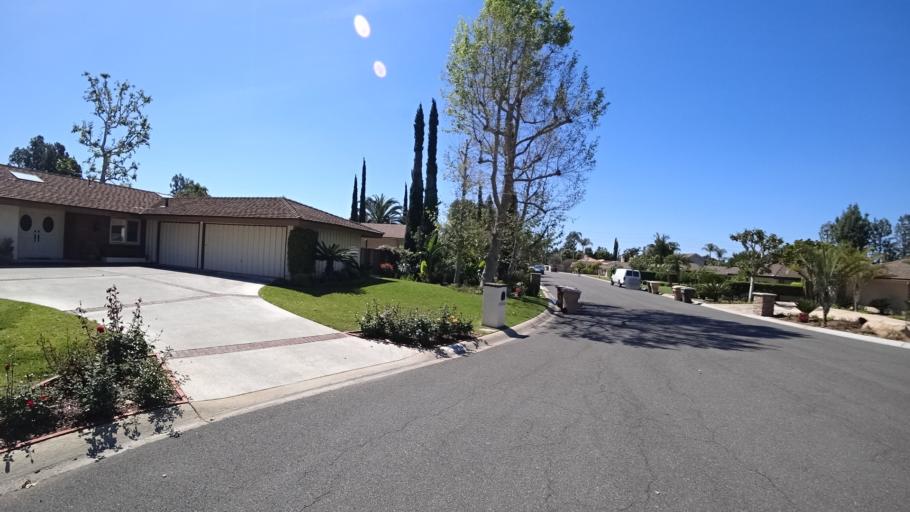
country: US
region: California
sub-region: Orange County
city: Villa Park
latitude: 33.8158
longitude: -117.8028
